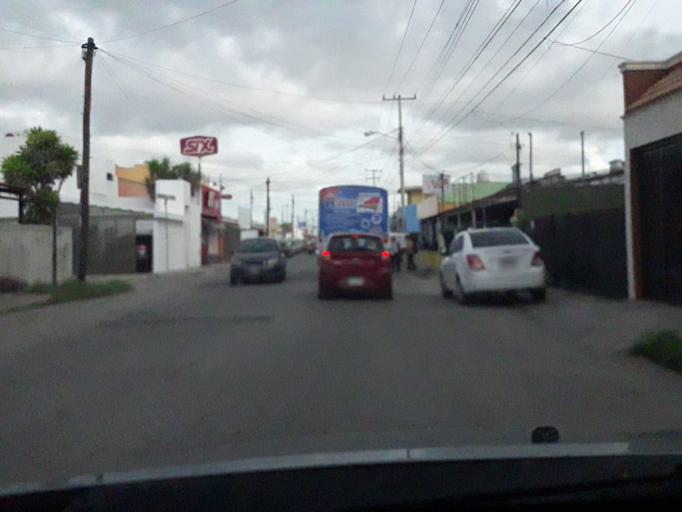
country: MX
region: Yucatan
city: Merida
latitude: 21.0214
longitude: -89.6417
